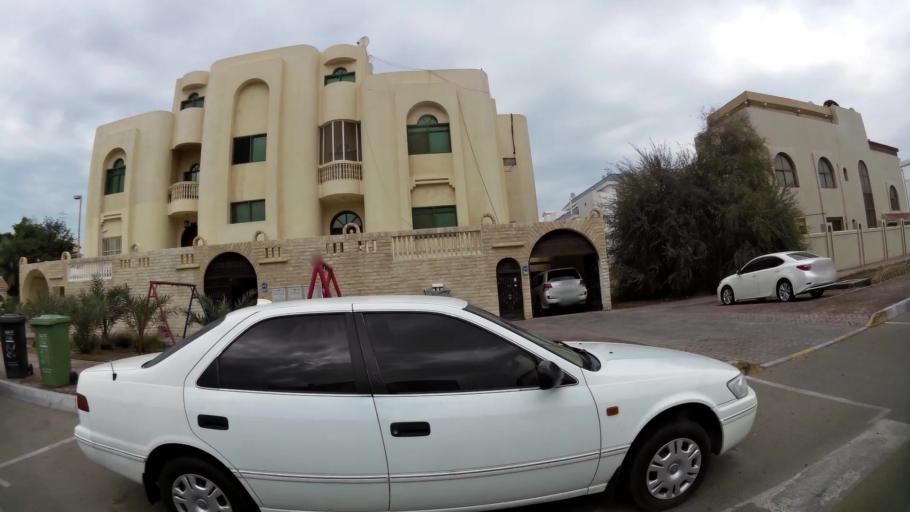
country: AE
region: Abu Dhabi
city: Abu Dhabi
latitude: 24.4405
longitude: 54.4033
